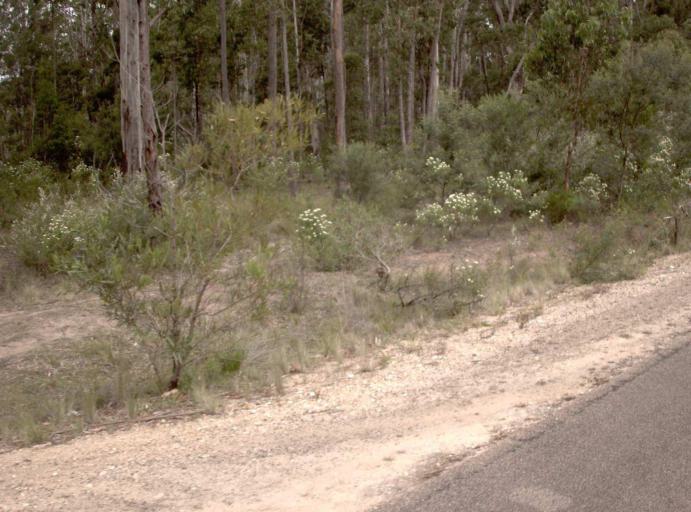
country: AU
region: Victoria
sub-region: East Gippsland
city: Lakes Entrance
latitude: -37.7117
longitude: 148.0729
